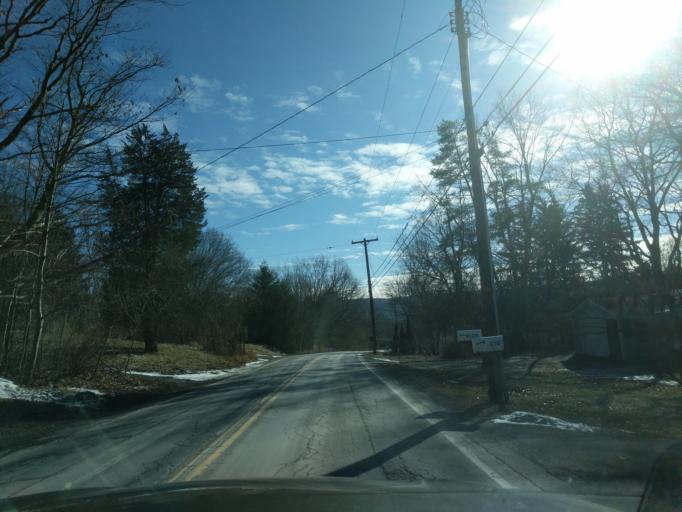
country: US
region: New York
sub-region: Tompkins County
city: East Ithaca
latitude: 42.4267
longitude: -76.4619
